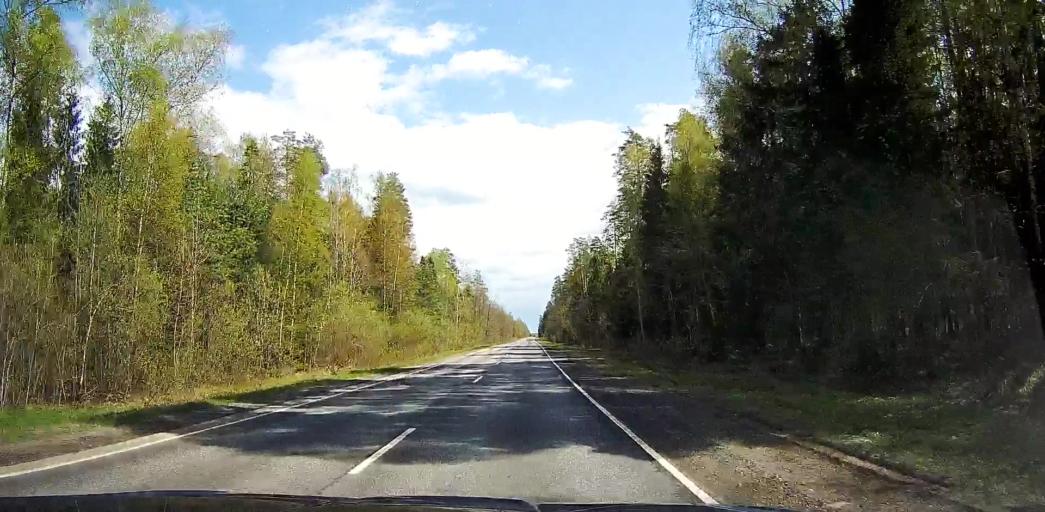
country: RU
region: Moskovskaya
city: Davydovo
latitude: 55.5515
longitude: 38.7658
